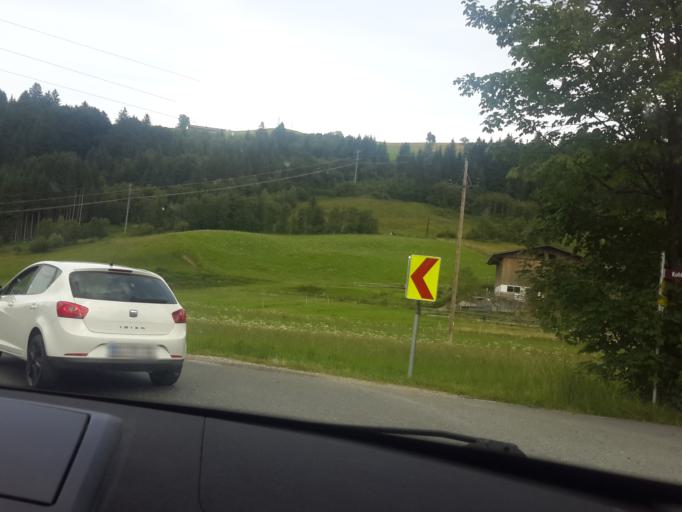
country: AT
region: Tyrol
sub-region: Politischer Bezirk Kitzbuhel
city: Reith bei Kitzbuhel
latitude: 47.4873
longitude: 12.3495
